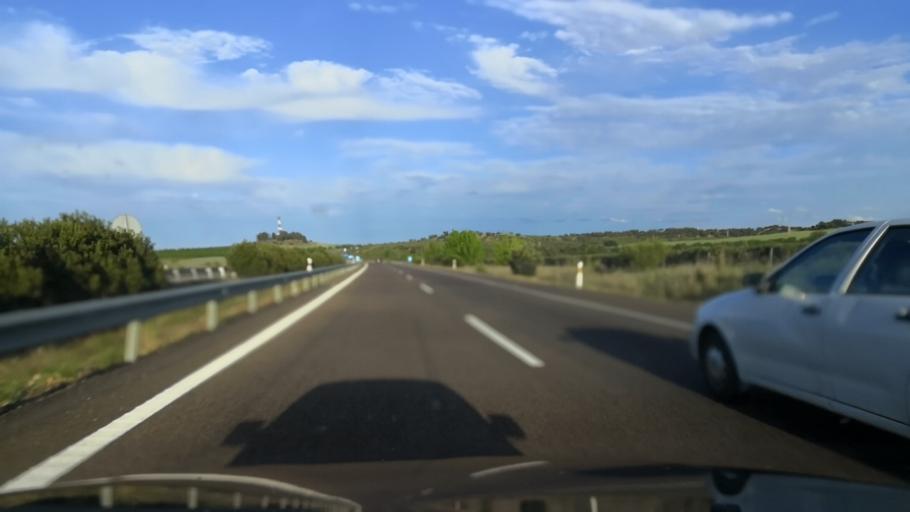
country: ES
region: Extremadura
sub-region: Provincia de Badajoz
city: Talavera La Real
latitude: 38.8683
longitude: -6.8395
